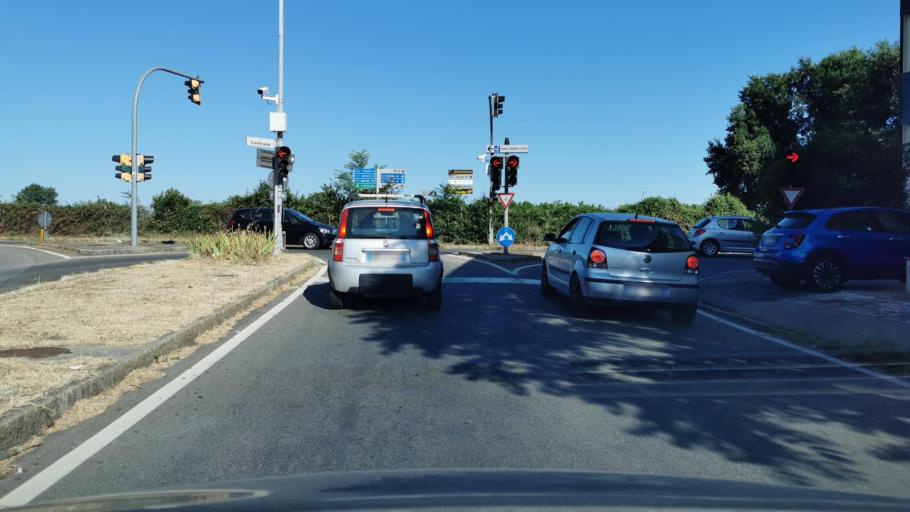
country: IT
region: Emilia-Romagna
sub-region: Provincia di Modena
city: Baggiovara
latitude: 44.6202
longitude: 10.8904
